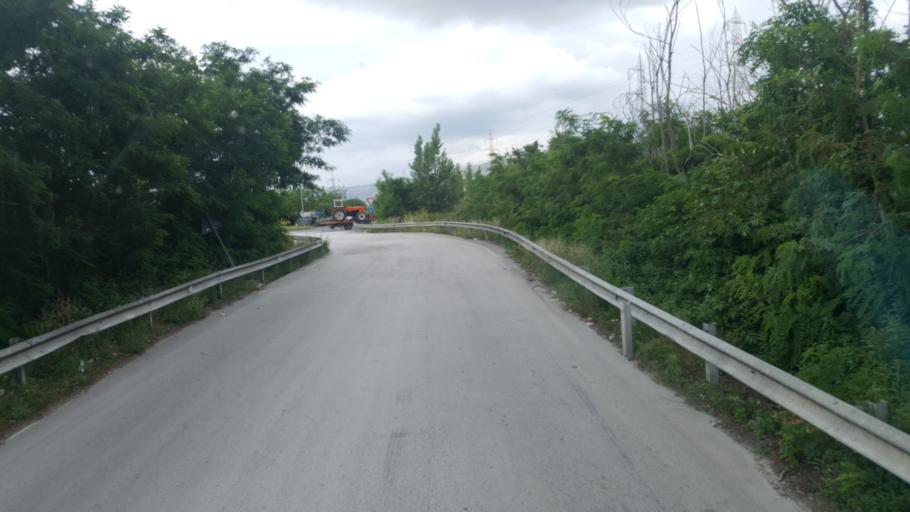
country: IT
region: Campania
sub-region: Provincia di Caserta
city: Maddaloni
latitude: 41.0131
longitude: 14.3712
